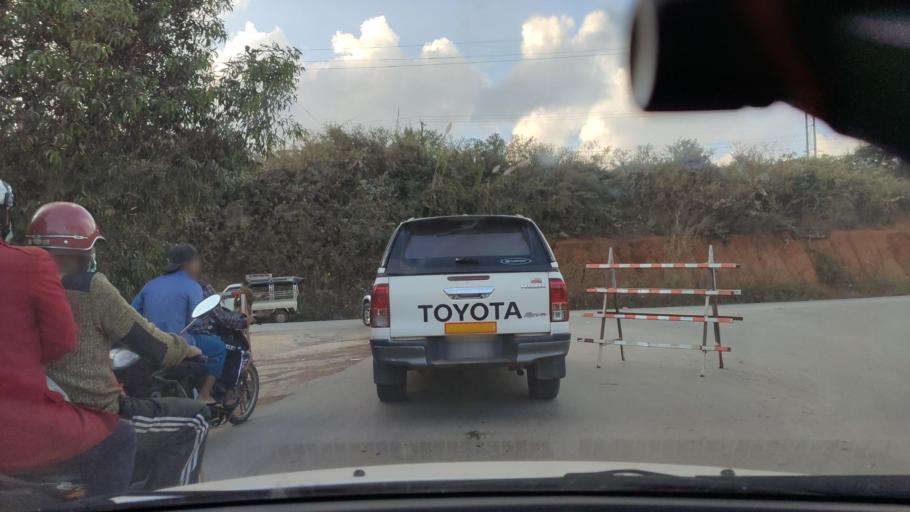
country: MM
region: Shan
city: Lashio
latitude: 22.8959
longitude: 97.7061
